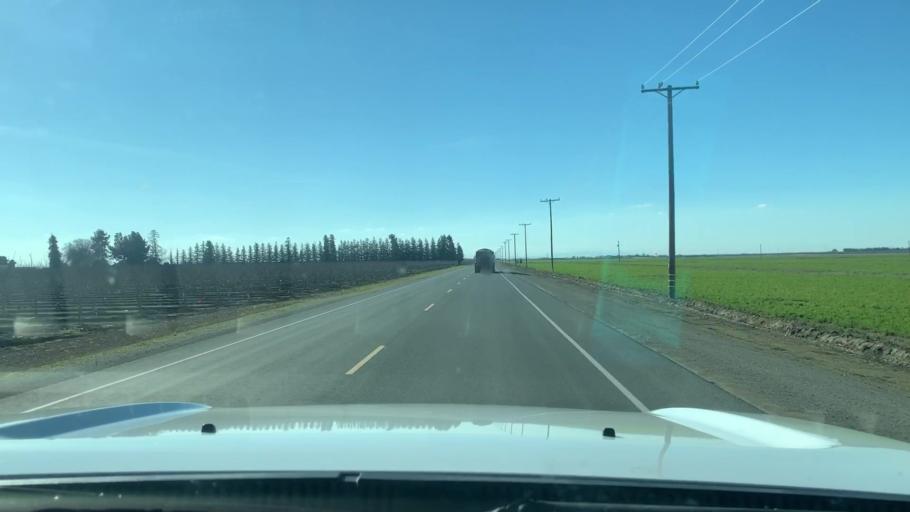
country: US
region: California
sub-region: Kings County
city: Corcoran
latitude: 36.2109
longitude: -119.4971
